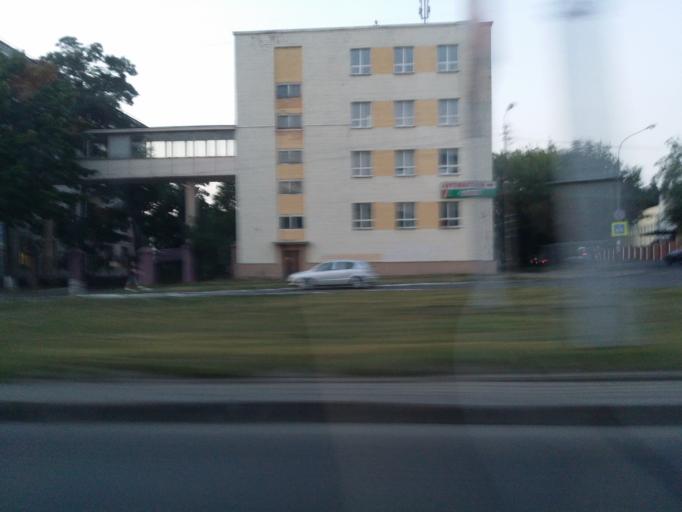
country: BY
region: Minsk
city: Minsk
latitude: 53.8732
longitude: 27.6373
